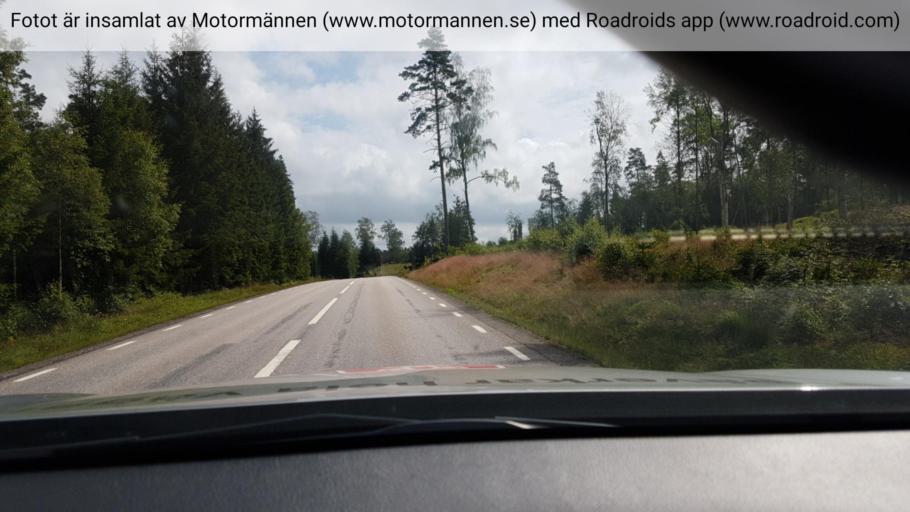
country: SE
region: Vaestra Goetaland
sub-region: Svenljunga Kommun
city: Svenljunga
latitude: 57.4802
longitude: 13.0320
